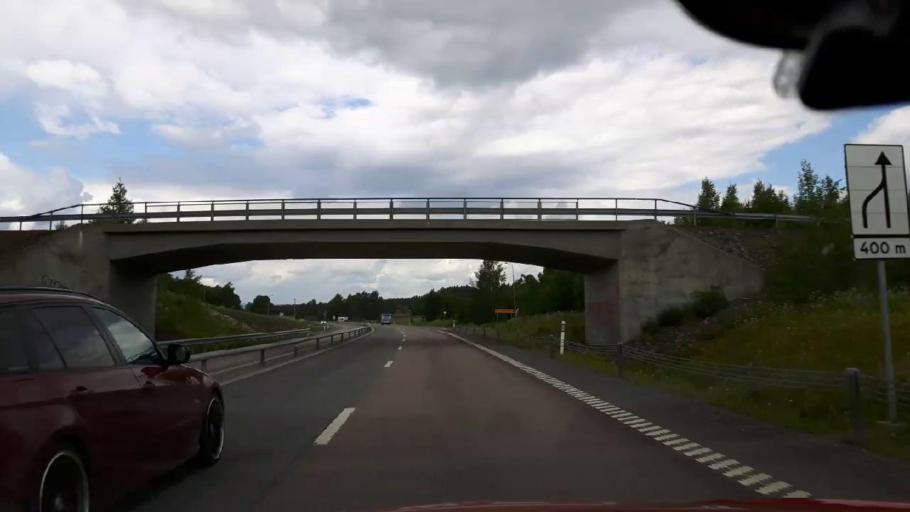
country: SE
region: Jaemtland
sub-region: Krokoms Kommun
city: Krokom
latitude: 63.3052
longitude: 14.4903
